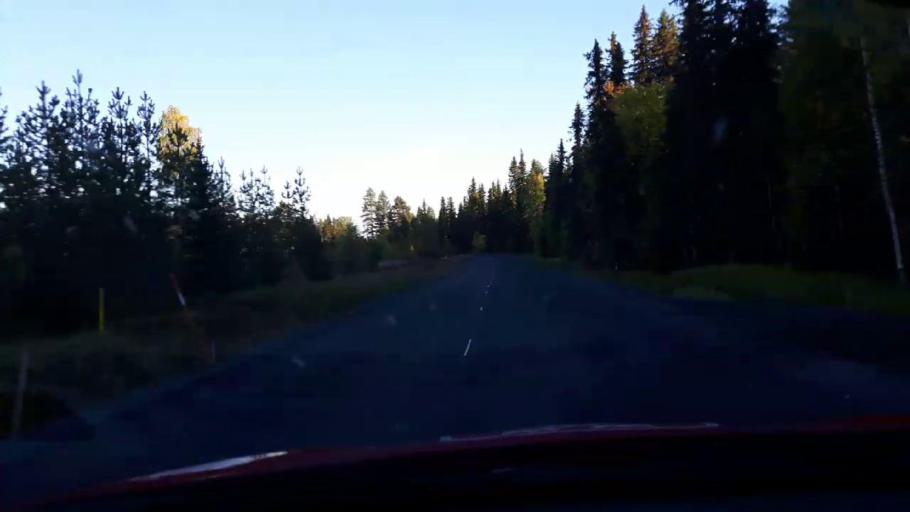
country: SE
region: Jaemtland
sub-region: OEstersunds Kommun
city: Lit
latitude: 63.4064
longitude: 14.8797
